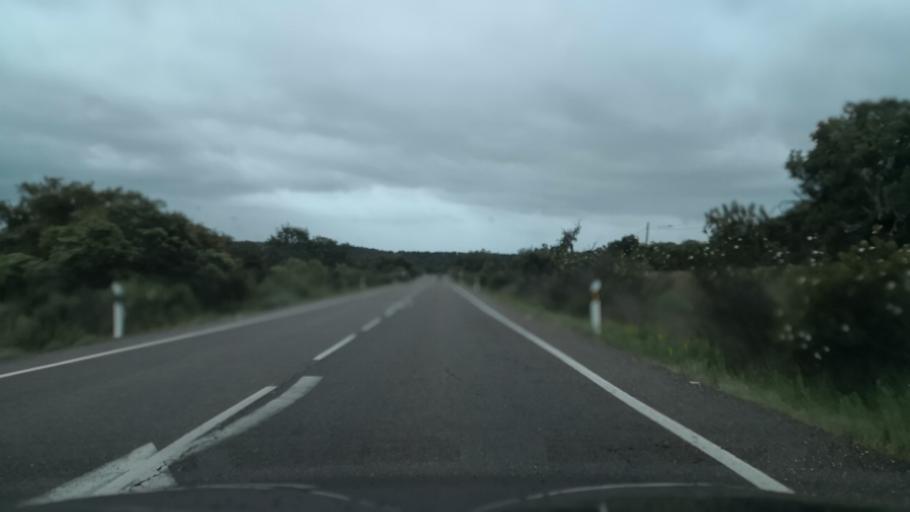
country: ES
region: Extremadura
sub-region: Provincia de Badajoz
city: Puebla de Obando
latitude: 39.1456
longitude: -6.6528
